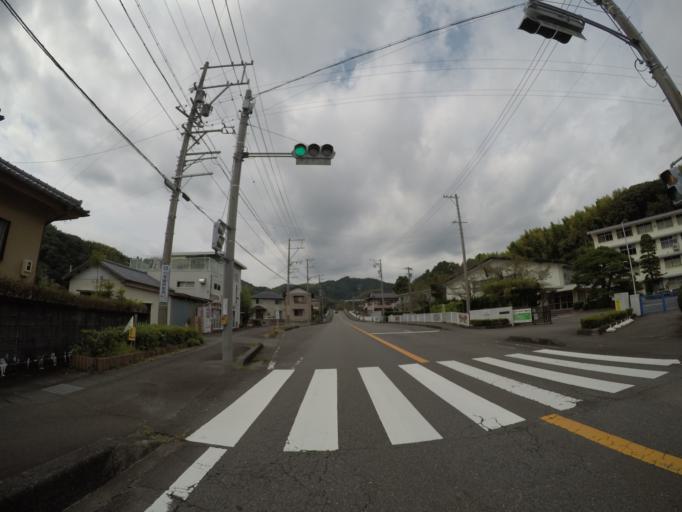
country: JP
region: Shizuoka
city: Fujieda
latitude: 34.8812
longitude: 138.2178
